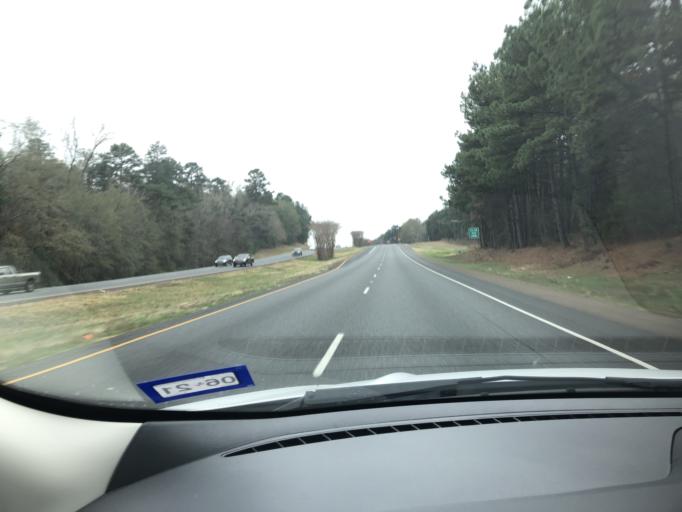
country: US
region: Texas
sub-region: Nacogdoches County
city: Nacogdoches
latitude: 31.5402
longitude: -94.6919
